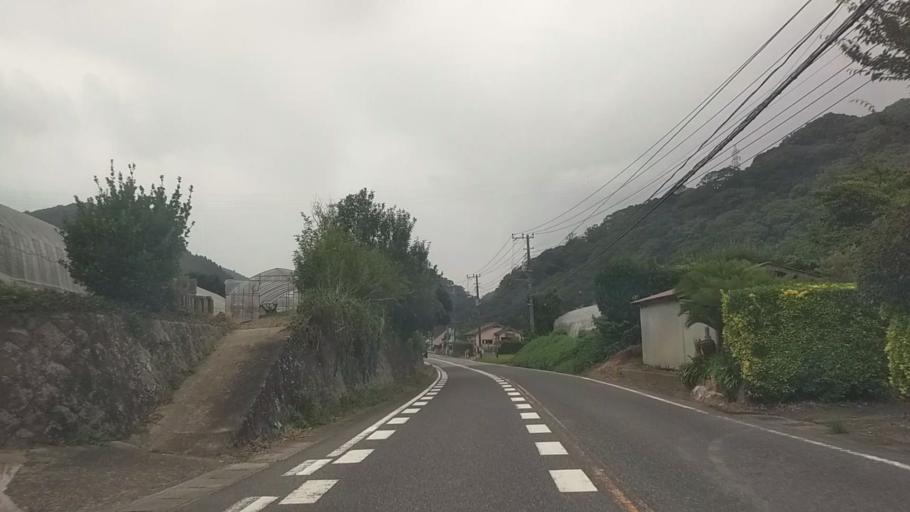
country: JP
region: Chiba
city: Tateyama
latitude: 35.1432
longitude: 139.8772
